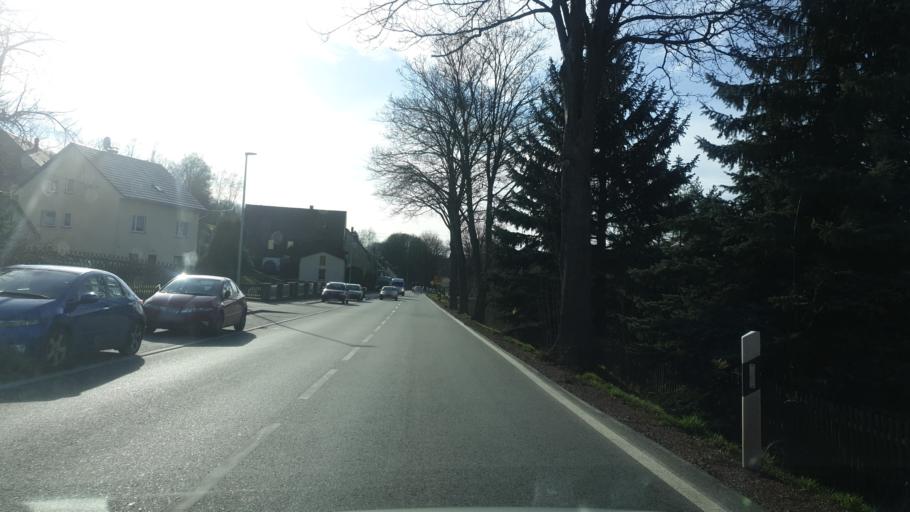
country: DE
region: Saxony
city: Hartenstein
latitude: 50.6683
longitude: 12.6525
